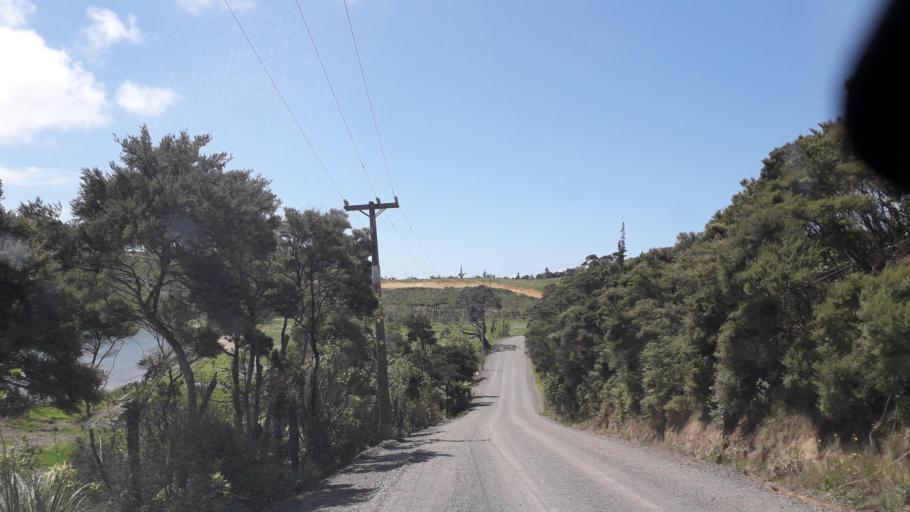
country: NZ
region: Northland
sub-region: Far North District
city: Paihia
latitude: -35.2414
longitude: 174.2479
